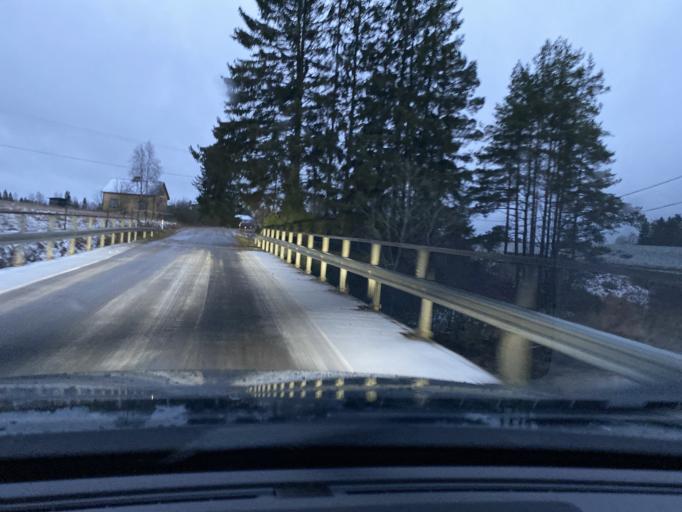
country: FI
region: Pirkanmaa
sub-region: Lounais-Pirkanmaa
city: Punkalaidun
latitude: 61.1222
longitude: 23.0282
